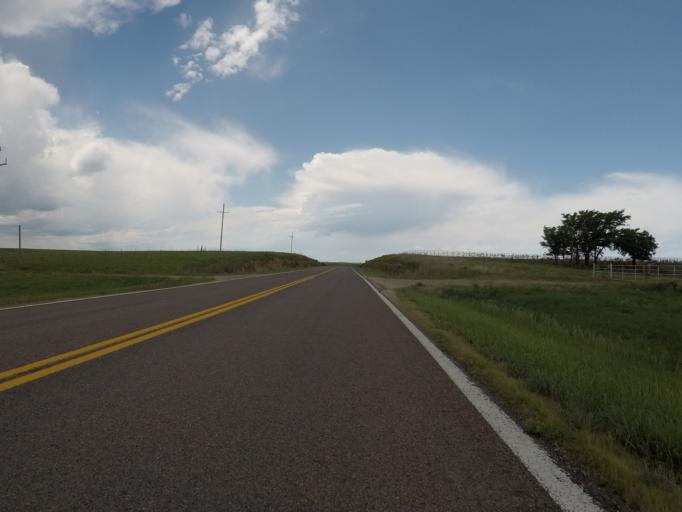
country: US
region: Kansas
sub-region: Wabaunsee County
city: Alma
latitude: 38.8697
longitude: -96.3347
